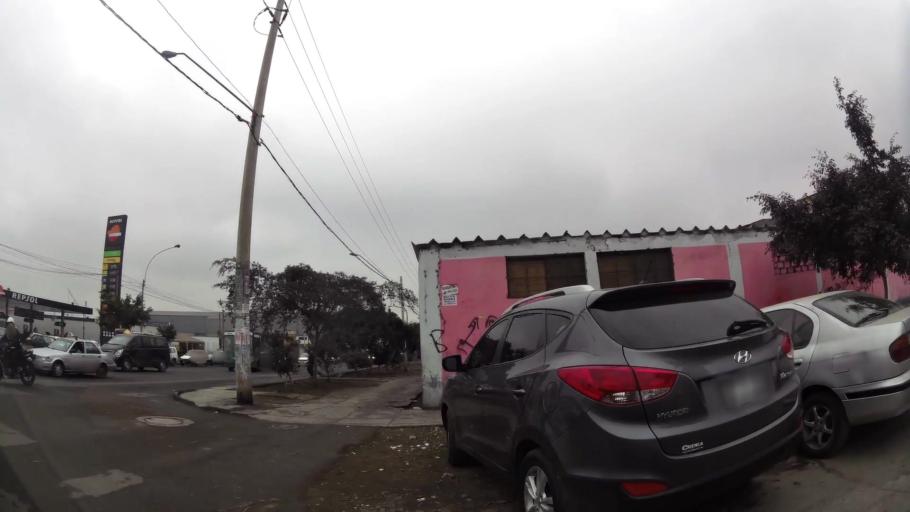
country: PE
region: Lima
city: Lima
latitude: -12.0633
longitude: -77.0205
